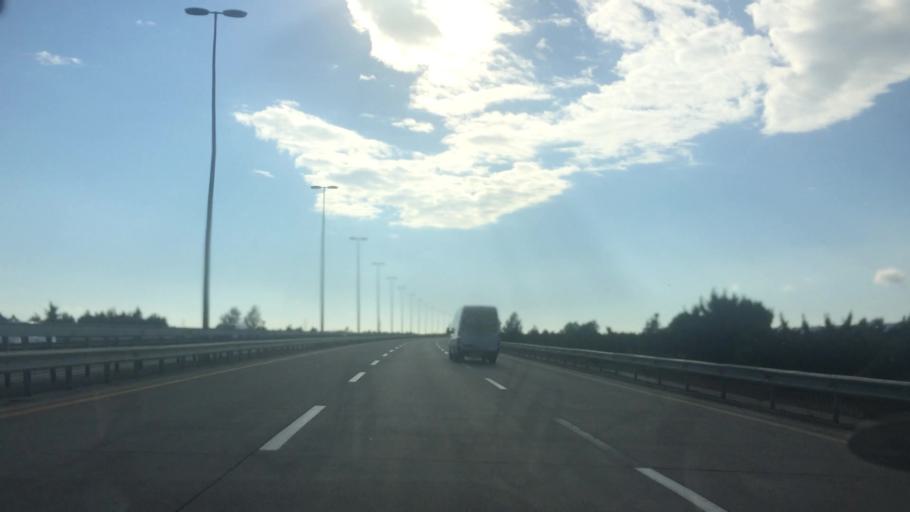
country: AZ
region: Baki
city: Hovsan
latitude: 40.3803
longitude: 50.0566
